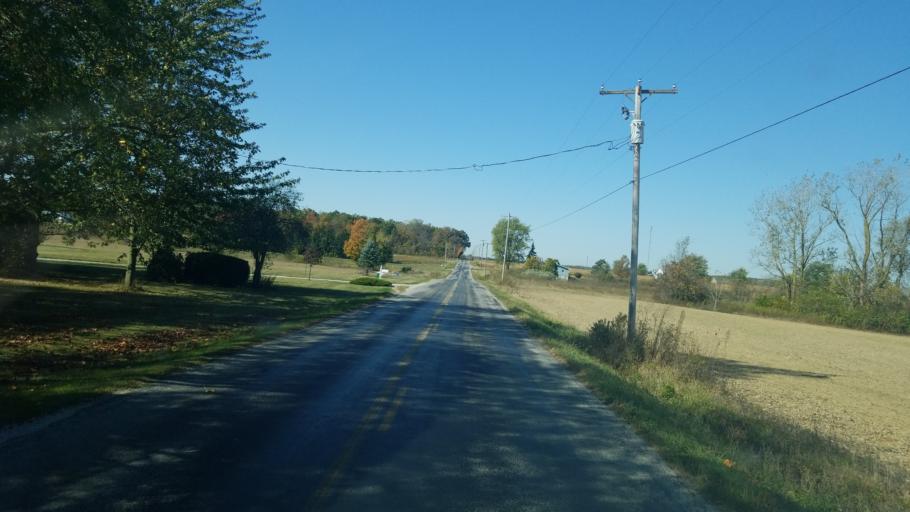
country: US
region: Ohio
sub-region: Delaware County
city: Ashley
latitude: 40.4568
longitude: -83.0322
